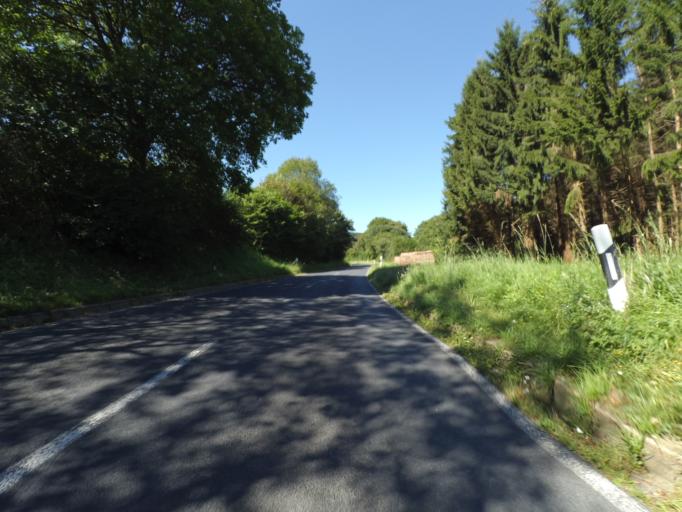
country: DE
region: Rheinland-Pfalz
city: Schutz
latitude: 50.1293
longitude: 6.7506
